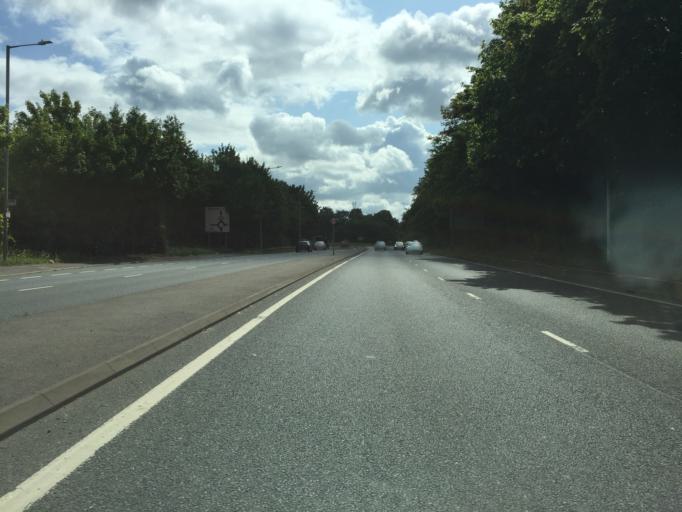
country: GB
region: England
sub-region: Kent
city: Aylesford
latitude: 51.2918
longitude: 0.4851
